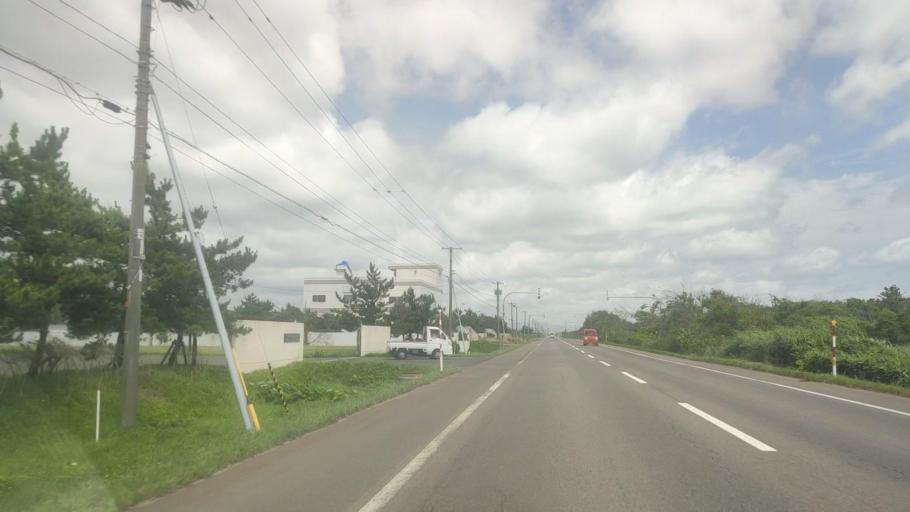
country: JP
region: Hokkaido
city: Niseko Town
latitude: 42.3861
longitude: 140.2961
